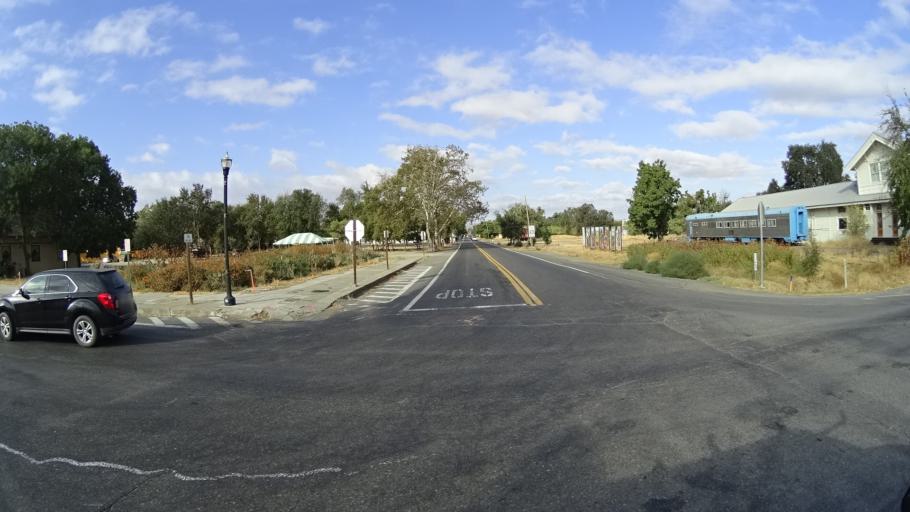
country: US
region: California
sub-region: Yolo County
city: Esparto
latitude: 38.6954
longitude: -122.0160
